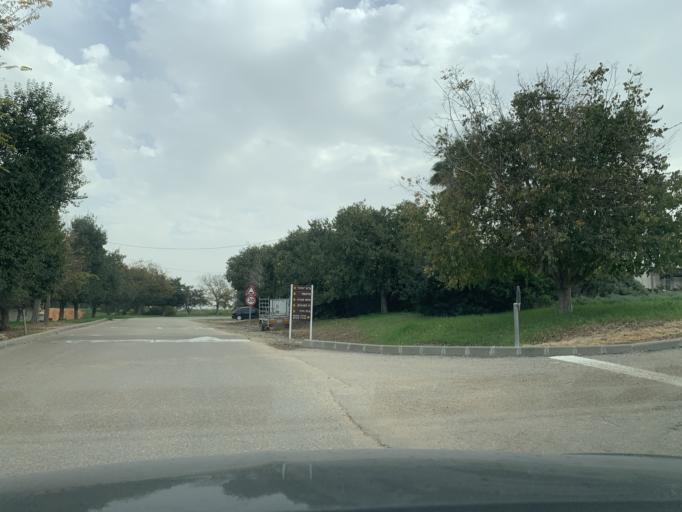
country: IL
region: Central District
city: Tirah
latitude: 32.2182
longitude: 34.9410
